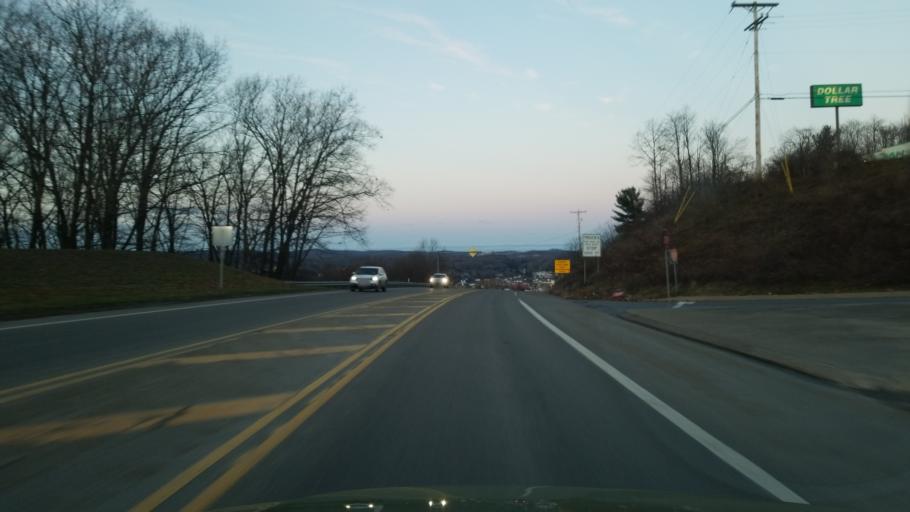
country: US
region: Pennsylvania
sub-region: Jefferson County
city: Punxsutawney
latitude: 40.9296
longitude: -78.9828
